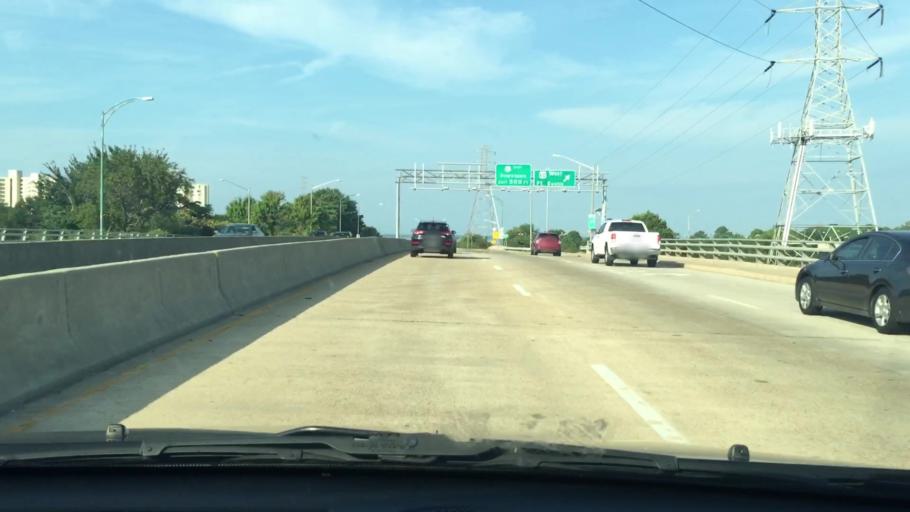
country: US
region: Virginia
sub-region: City of Newport News
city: Newport News
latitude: 37.0182
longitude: -76.4483
